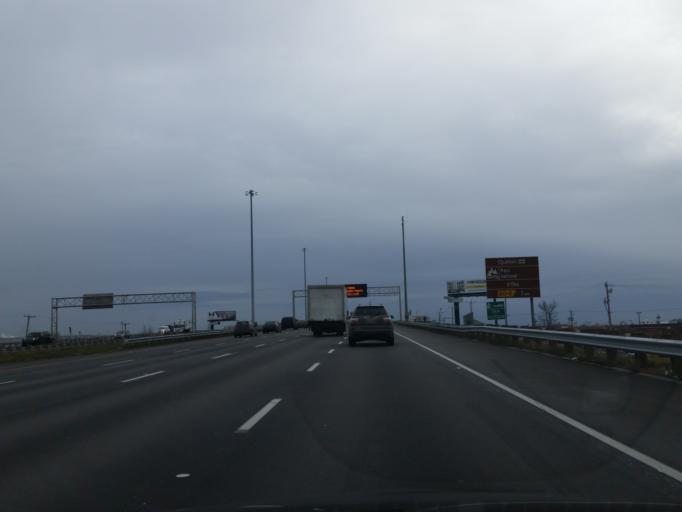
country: CA
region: Quebec
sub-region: Laurentides
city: Sainte-Therese
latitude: 45.6373
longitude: -73.8554
